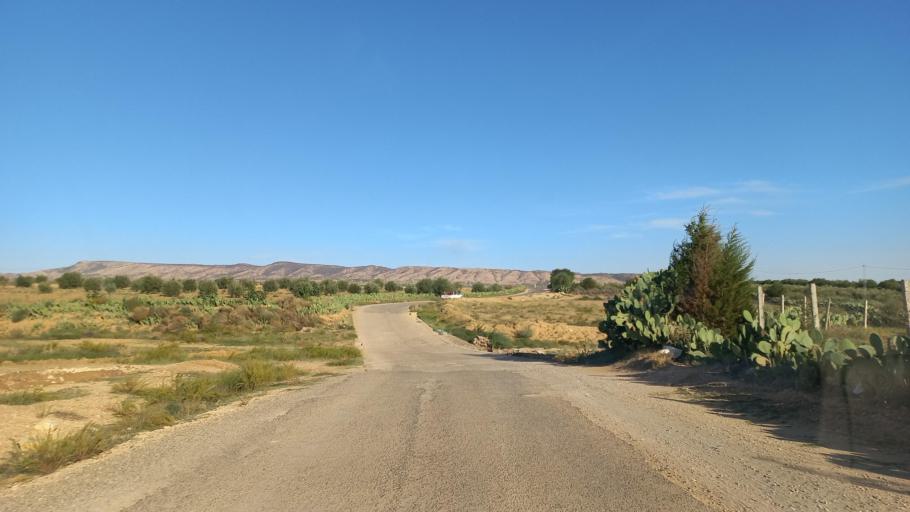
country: TN
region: Al Qasrayn
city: Sbiba
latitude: 35.3349
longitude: 9.0881
